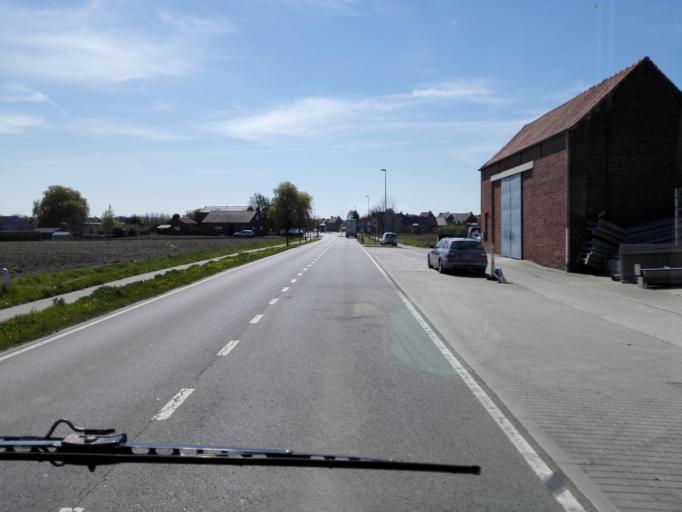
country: BE
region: Flanders
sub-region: Provincie West-Vlaanderen
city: Ingelmunster
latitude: 50.9332
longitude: 3.2644
